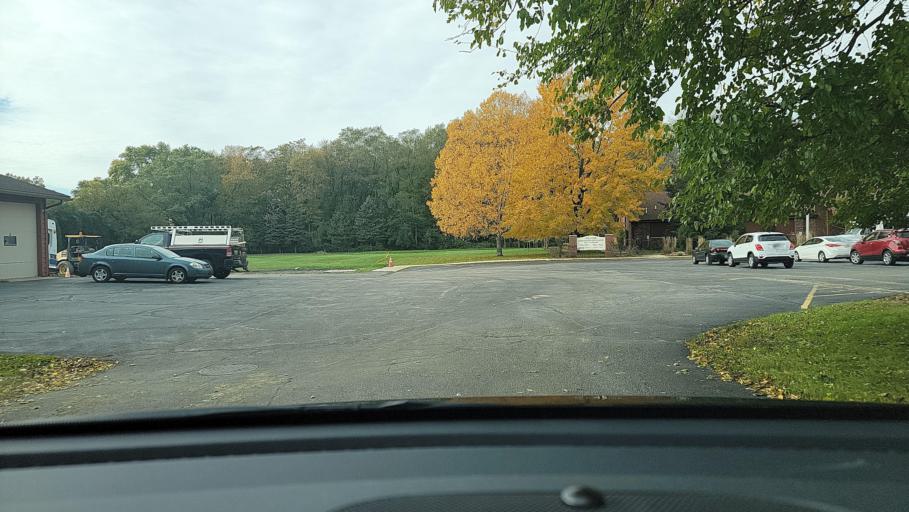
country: US
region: Indiana
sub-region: Porter County
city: Portage
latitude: 41.5727
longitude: -87.1894
